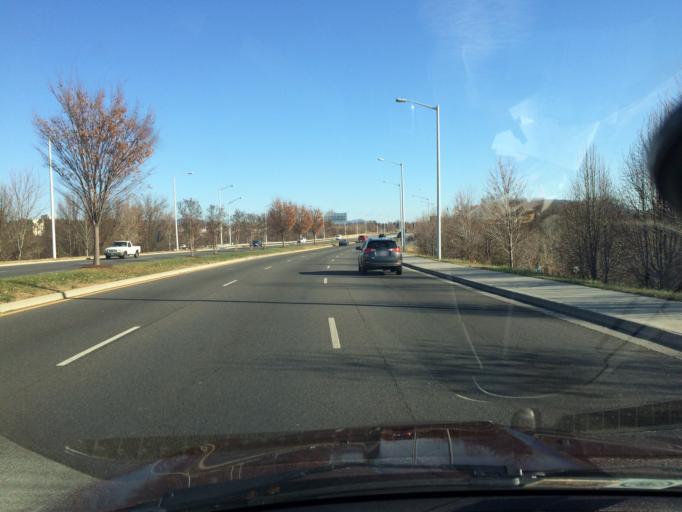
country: US
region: Virginia
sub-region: Roanoke County
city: Hollins
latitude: 37.3070
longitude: -79.9765
